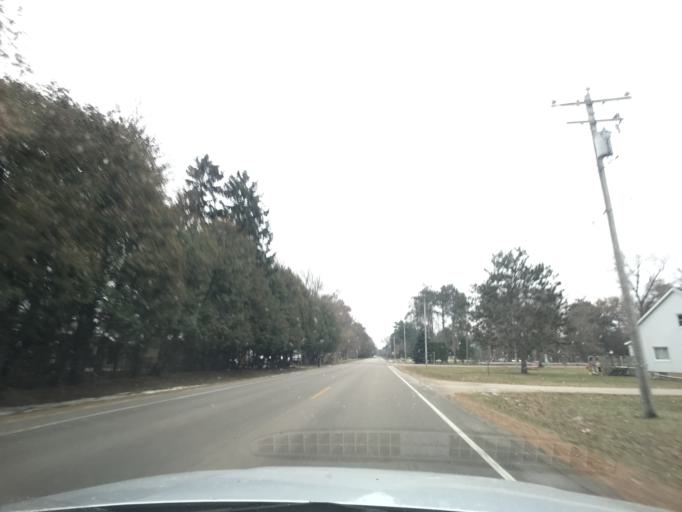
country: US
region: Wisconsin
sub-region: Marinette County
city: Marinette
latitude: 45.0572
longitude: -87.6213
